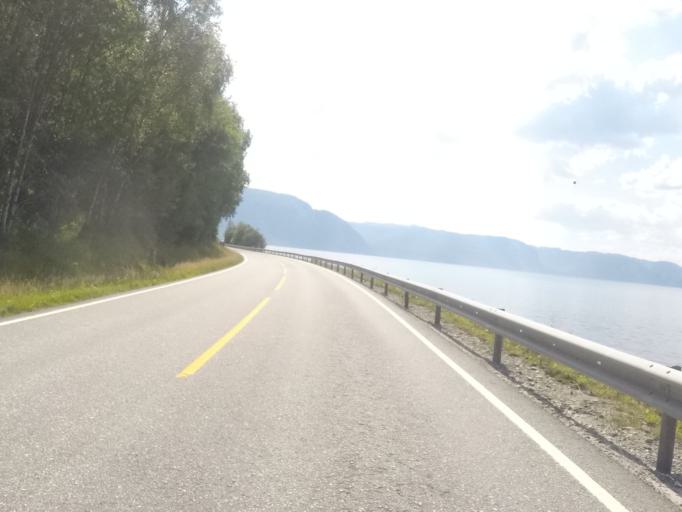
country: NO
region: Sogn og Fjordane
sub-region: Gaular
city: Sande
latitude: 61.1486
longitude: 5.6247
